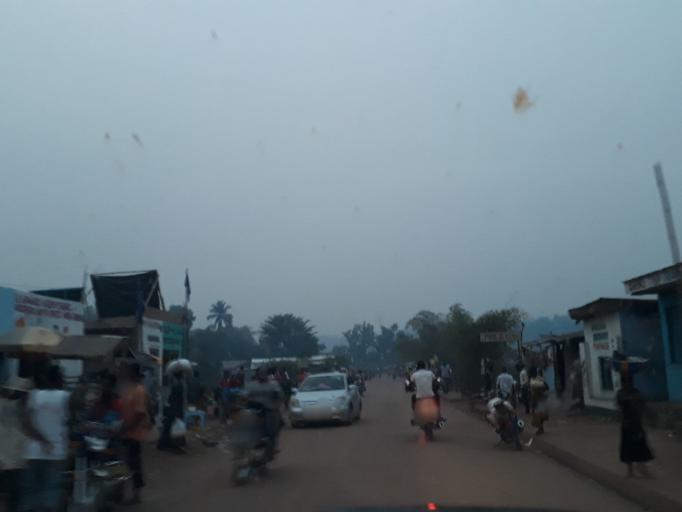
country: CD
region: Bandundu
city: Kikwit
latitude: -5.0430
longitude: 18.8371
